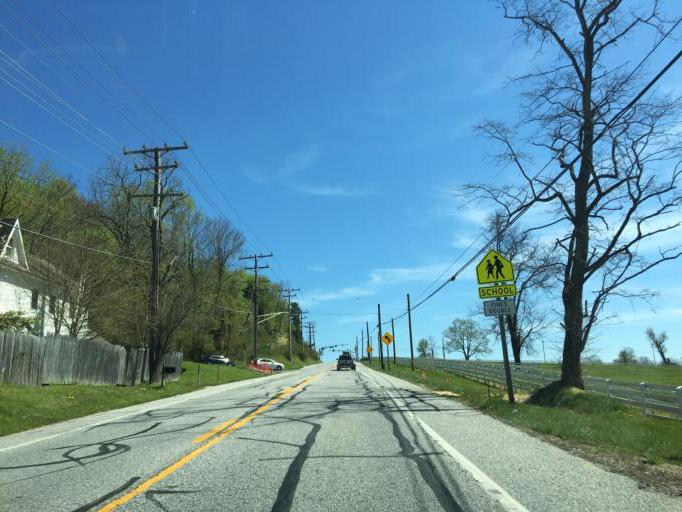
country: US
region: Maryland
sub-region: Baltimore County
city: Hunt Valley
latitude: 39.5719
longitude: -76.6590
